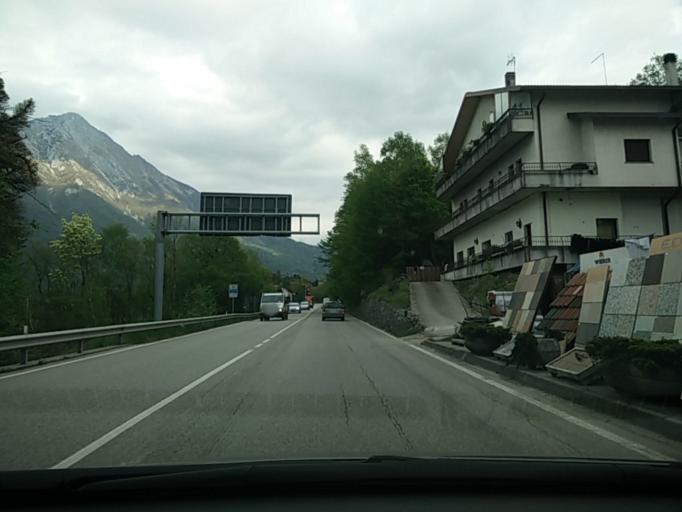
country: IT
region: Veneto
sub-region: Provincia di Belluno
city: Ponte nell'Alpi
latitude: 46.1723
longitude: 12.2859
